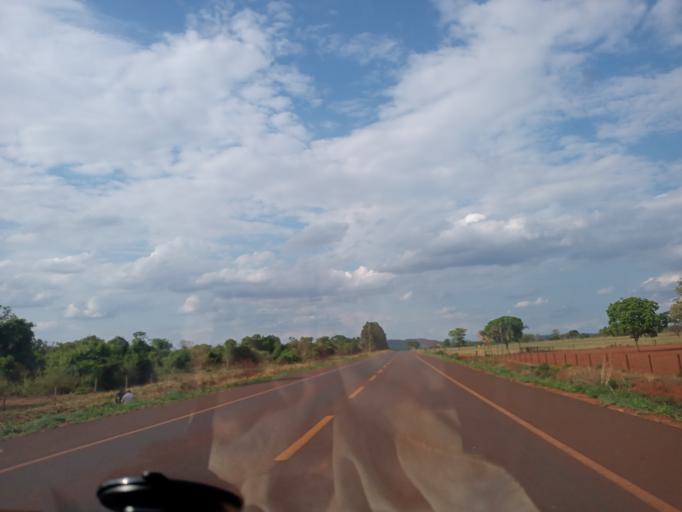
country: BR
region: Minas Gerais
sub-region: Ituiutaba
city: Ituiutaba
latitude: -19.0758
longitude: -49.5044
